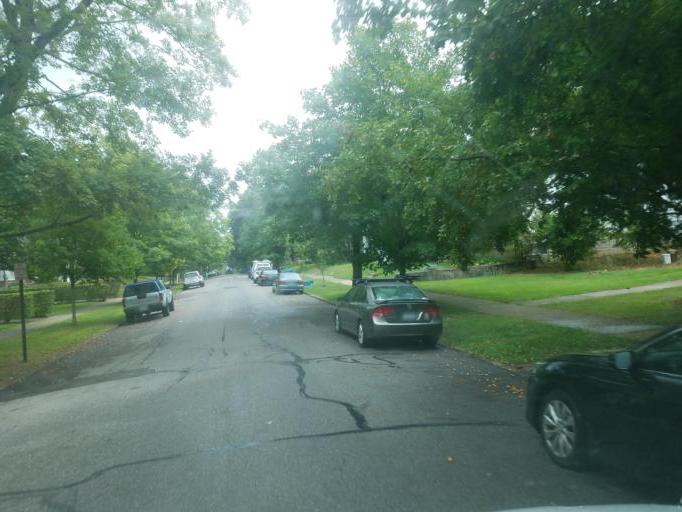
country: US
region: Ohio
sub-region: Delaware County
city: Delaware
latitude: 40.3036
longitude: -83.0691
